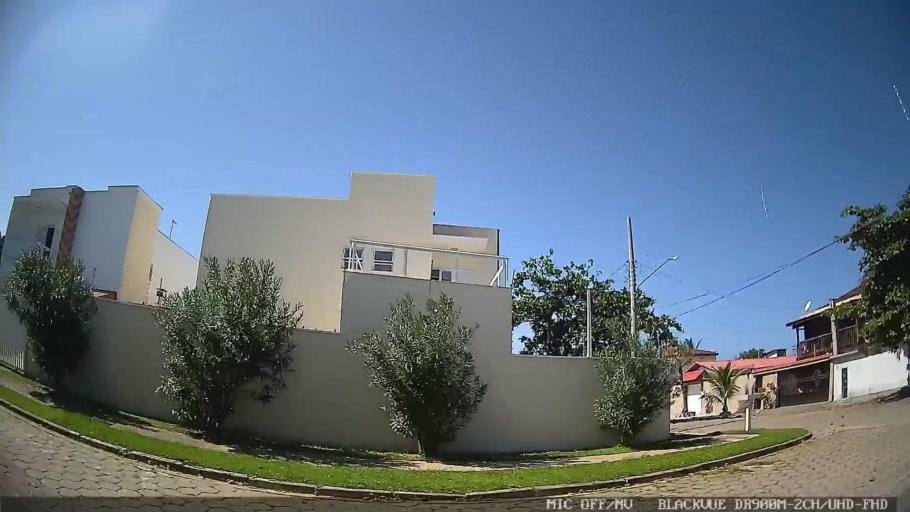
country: BR
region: Sao Paulo
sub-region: Peruibe
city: Peruibe
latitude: -24.3148
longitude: -46.9931
